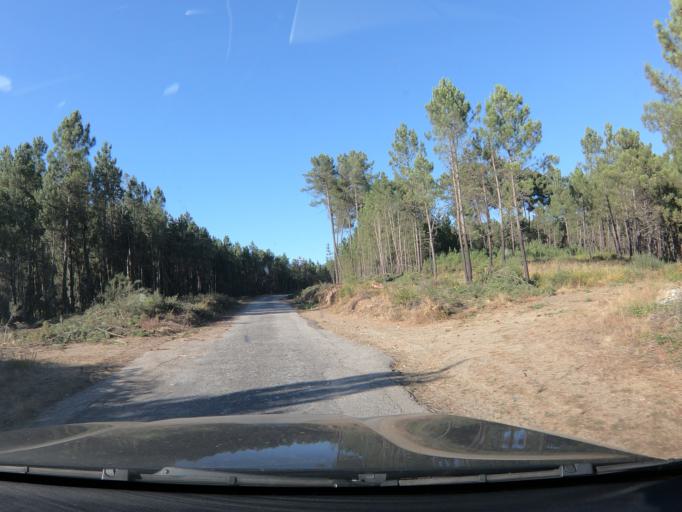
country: PT
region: Vila Real
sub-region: Sabrosa
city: Vilela
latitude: 41.2512
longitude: -7.6261
